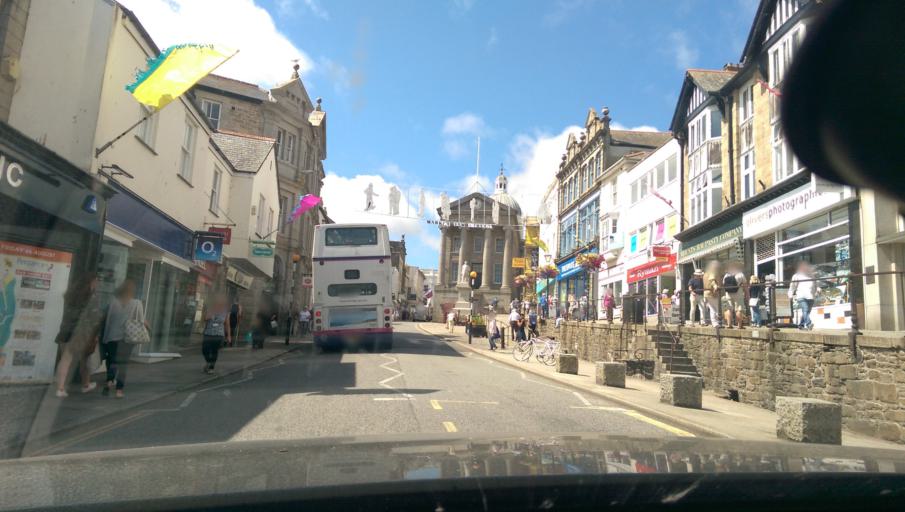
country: GB
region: England
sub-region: Cornwall
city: Penzance
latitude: 50.1194
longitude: -5.5356
